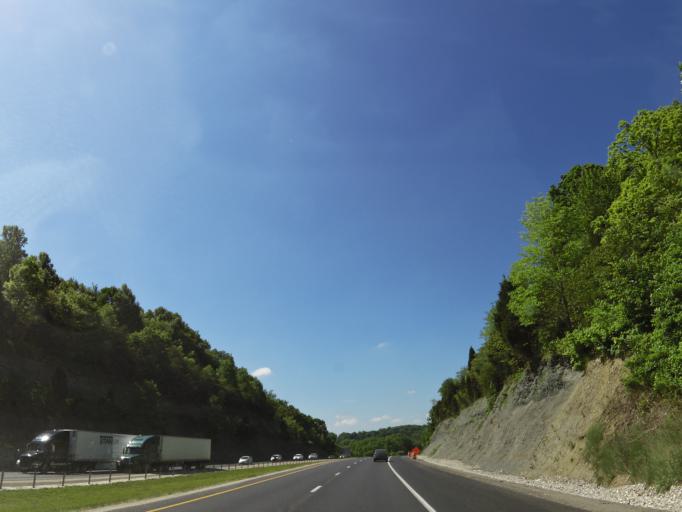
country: US
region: Kentucky
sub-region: Rockcastle County
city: Brodhead
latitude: 37.4521
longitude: -84.3359
